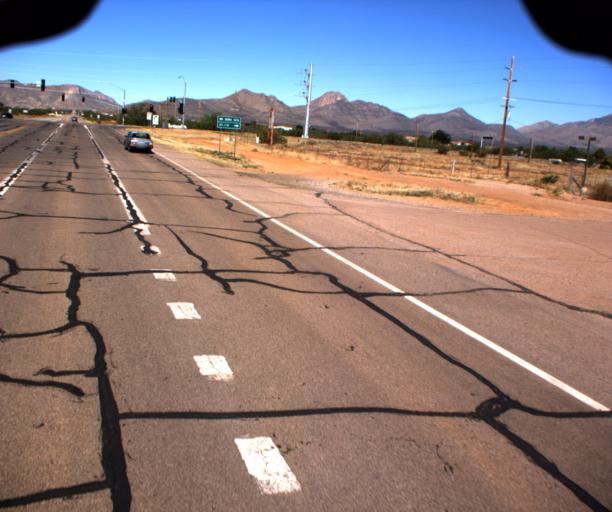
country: US
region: Arizona
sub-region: Cochise County
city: Huachuca City
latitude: 31.6928
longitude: -110.3488
